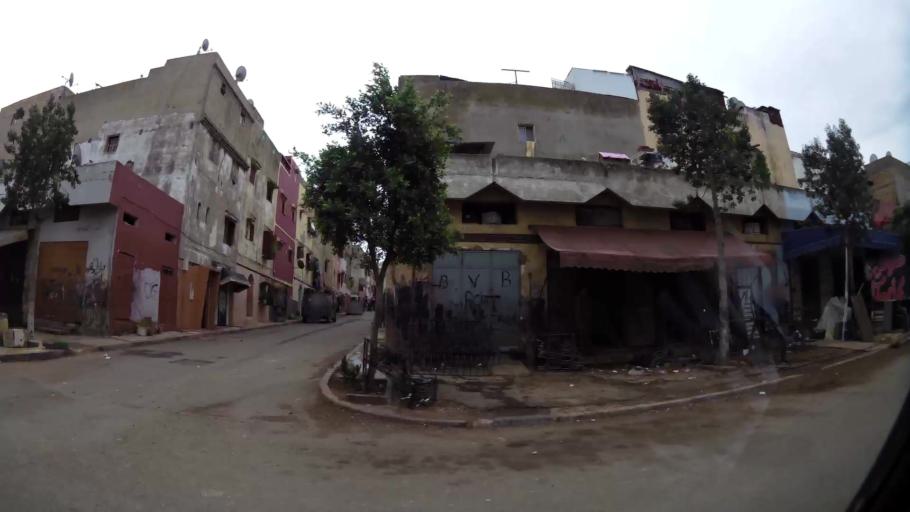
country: MA
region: Grand Casablanca
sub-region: Mediouna
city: Tit Mellil
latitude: 33.5695
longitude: -7.5428
